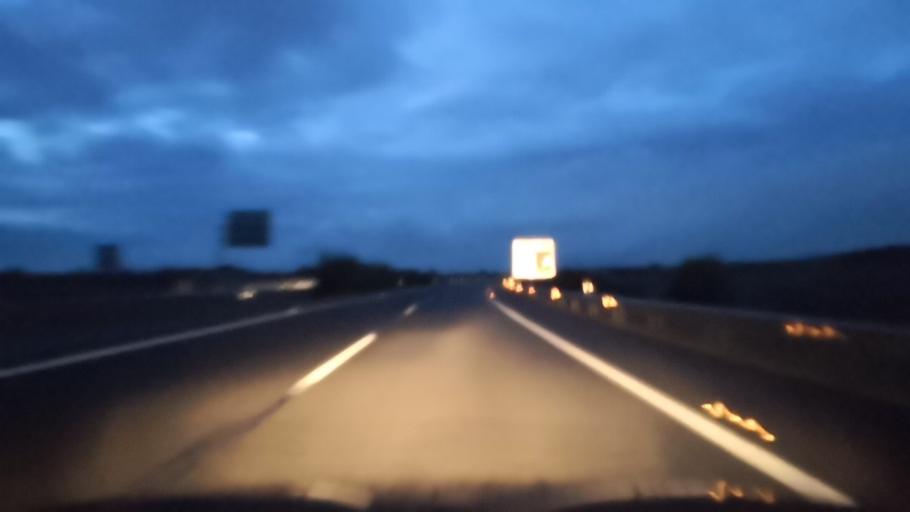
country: ES
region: Extremadura
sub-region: Provincia de Caceres
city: Caceres
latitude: 39.4389
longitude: -6.4113
